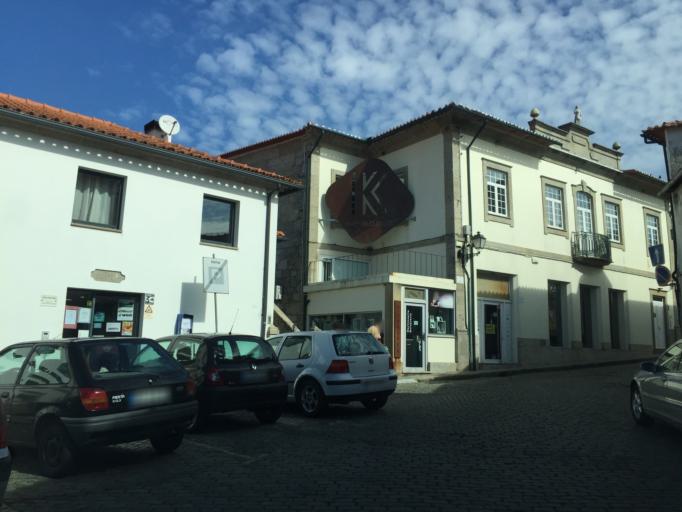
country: PT
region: Aveiro
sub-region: Castelo de Paiva
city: Castelo de Paiva
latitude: 41.0410
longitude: -8.2709
